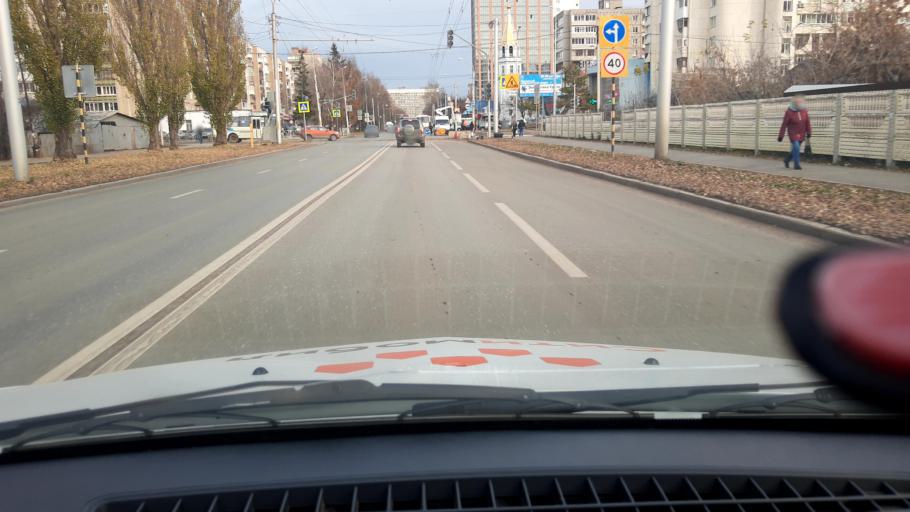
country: RU
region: Bashkortostan
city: Ufa
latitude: 54.7801
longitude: 56.1313
